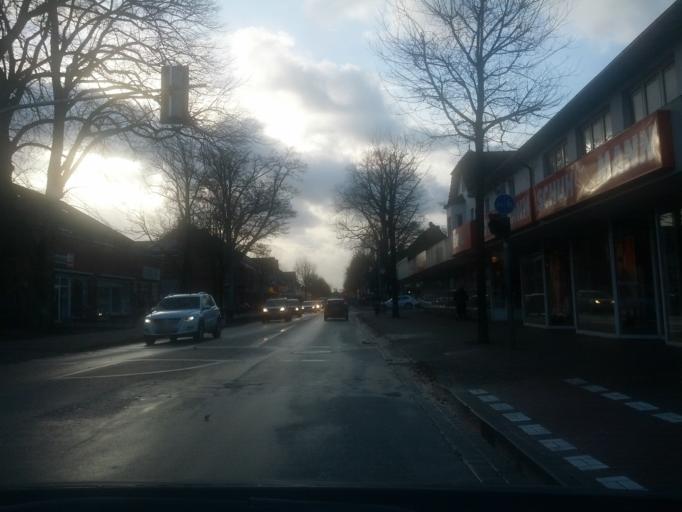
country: DE
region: Lower Saxony
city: Sittensen
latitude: 53.2824
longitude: 9.5057
